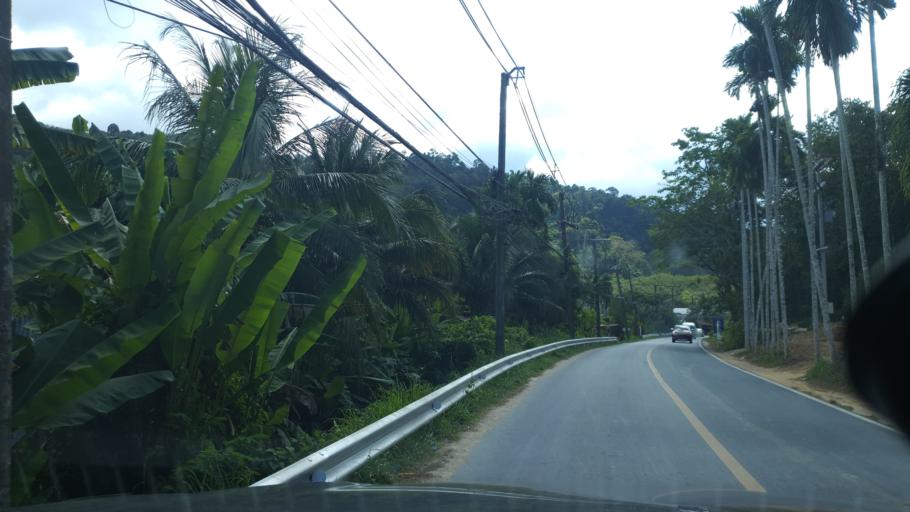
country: TH
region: Phuket
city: Thalang
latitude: 8.0682
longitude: 98.2935
